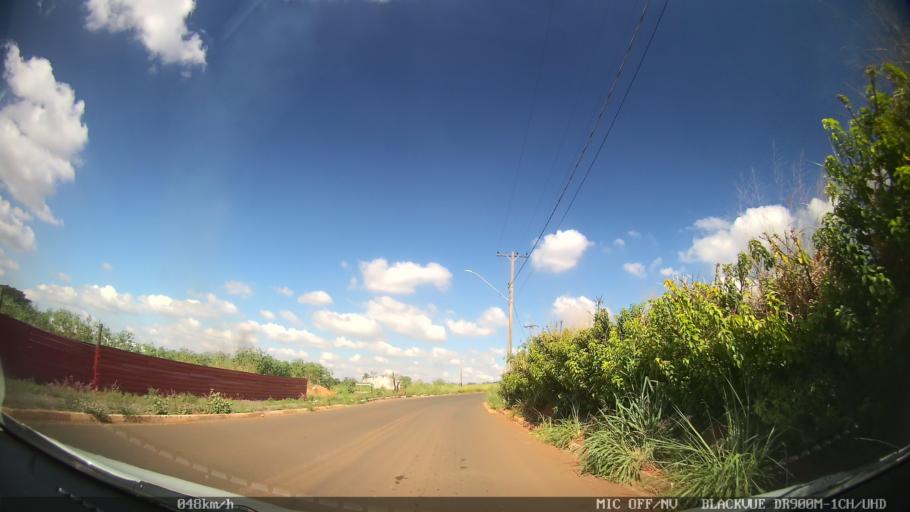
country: BR
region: Sao Paulo
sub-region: Hortolandia
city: Hortolandia
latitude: -22.8768
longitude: -47.2423
